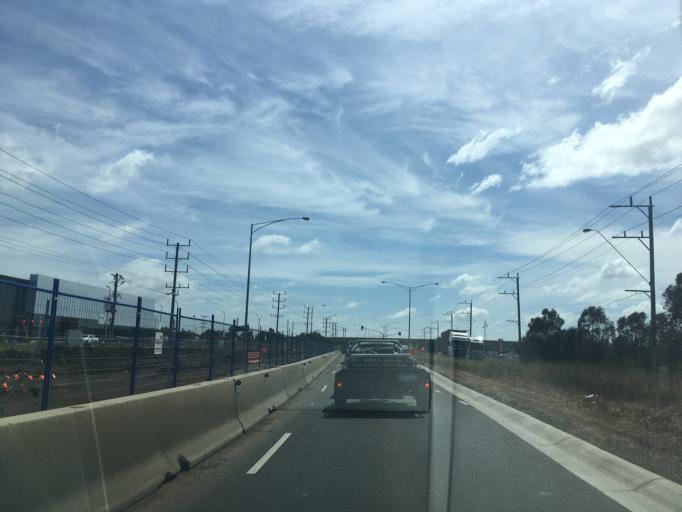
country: AU
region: Victoria
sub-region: Wyndham
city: Truganina
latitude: -37.8011
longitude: 144.7521
